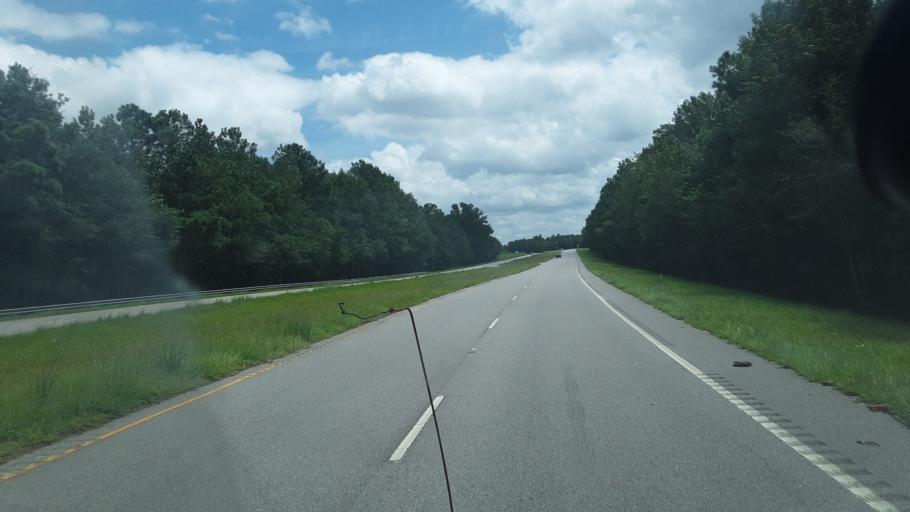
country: US
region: North Carolina
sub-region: Columbus County
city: Tabor City
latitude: 34.1162
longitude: -78.9669
